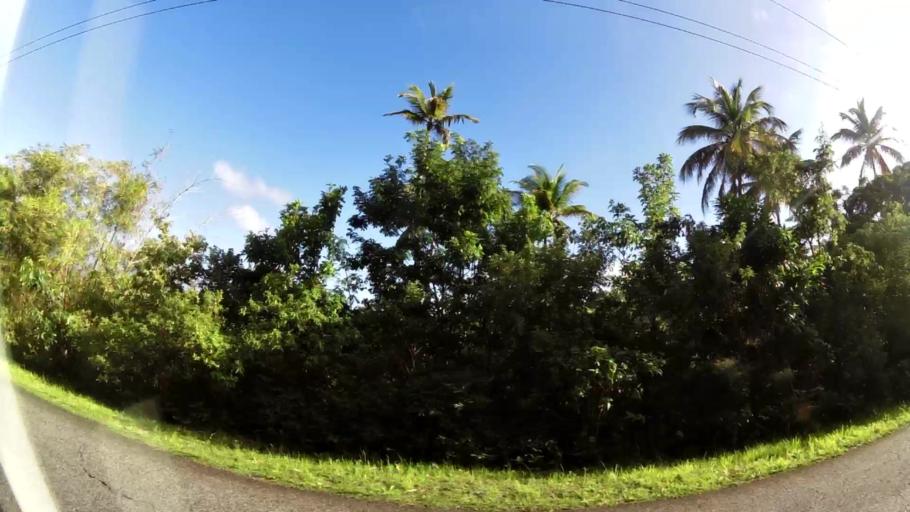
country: LC
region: Anse-la-Raye
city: Canaries
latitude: 13.9161
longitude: -61.0497
